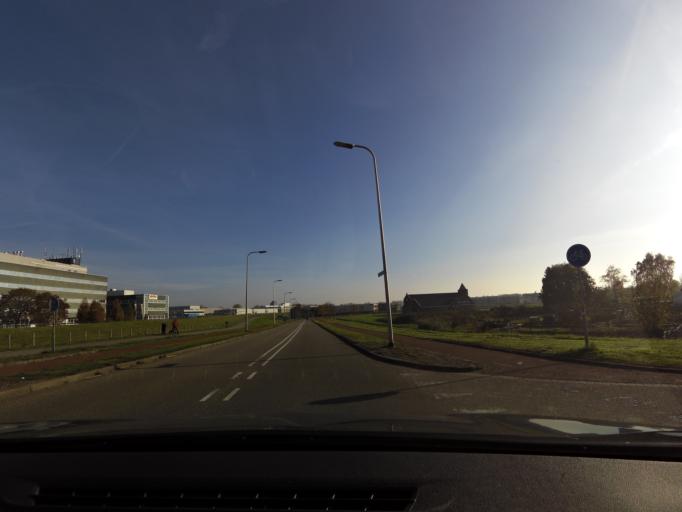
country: NL
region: South Holland
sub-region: Gemeente Ridderkerk
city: Ridderkerk
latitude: 51.8848
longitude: 4.6157
